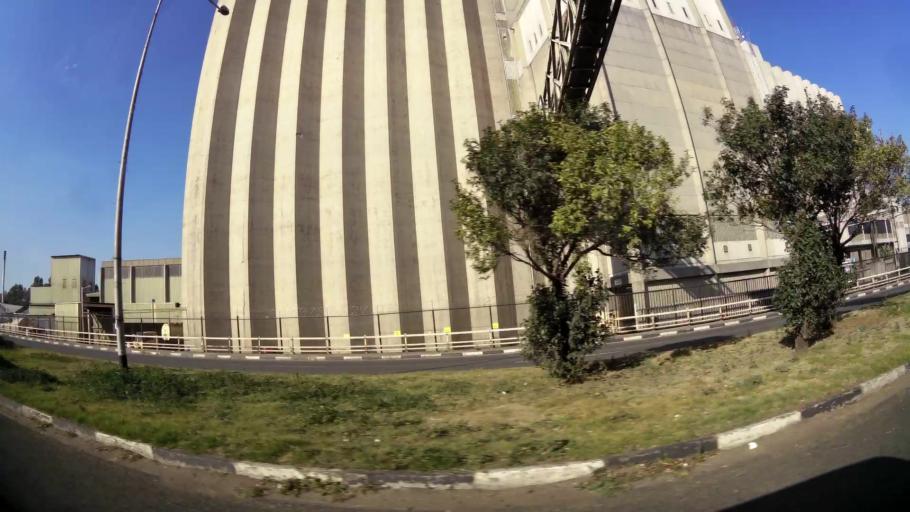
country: ZA
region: Gauteng
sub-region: West Rand District Municipality
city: Randfontein
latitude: -26.1648
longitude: 27.7125
